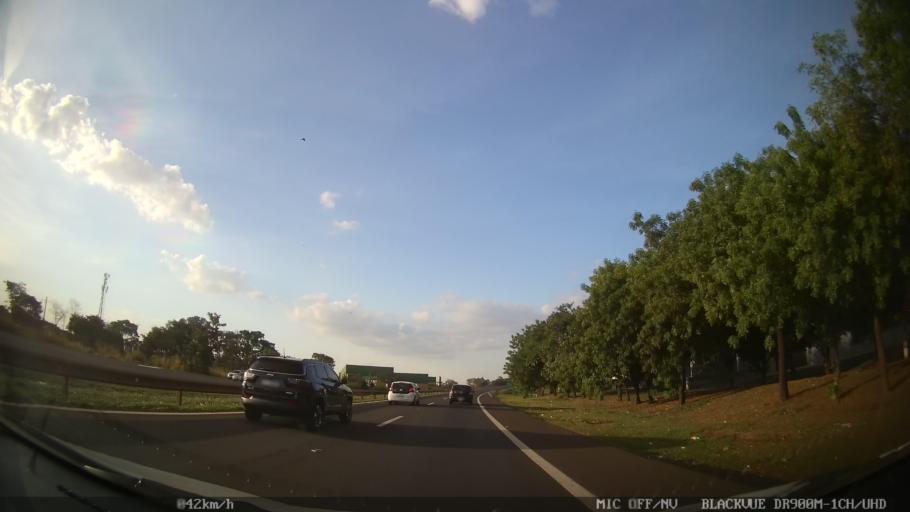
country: BR
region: Sao Paulo
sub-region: Ribeirao Preto
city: Ribeirao Preto
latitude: -21.1179
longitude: -47.7849
